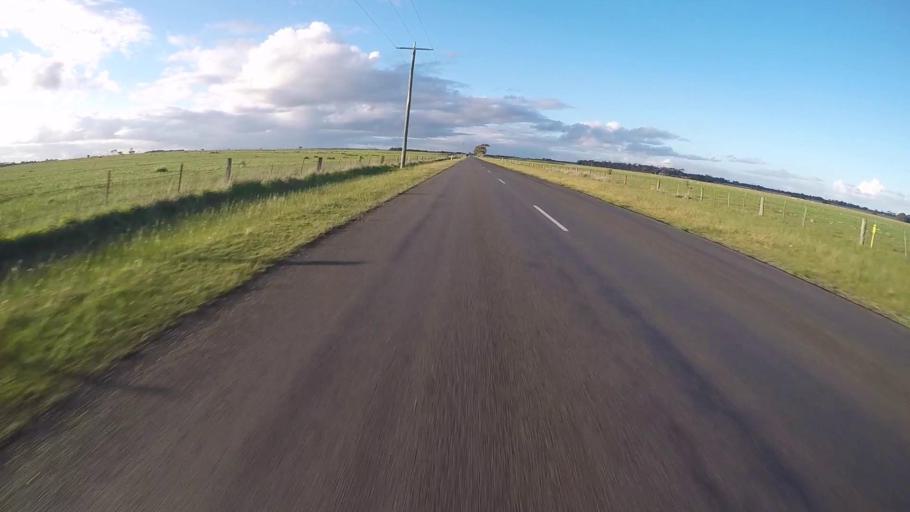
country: AU
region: Victoria
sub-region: Greater Geelong
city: Wandana Heights
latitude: -38.1332
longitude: 144.2003
